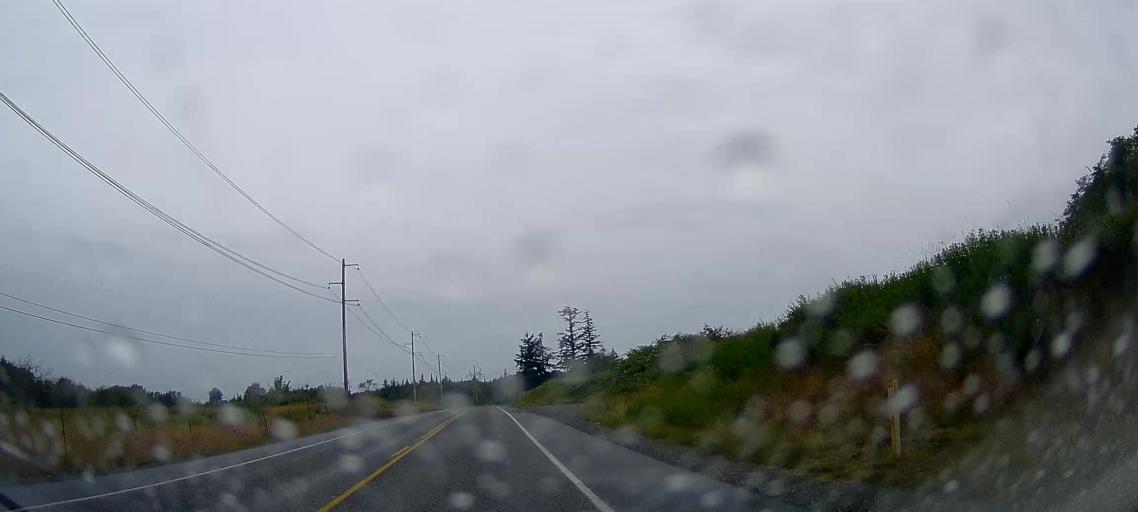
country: US
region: Washington
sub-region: Whatcom County
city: Birch Bay
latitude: 48.8521
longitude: -122.6979
